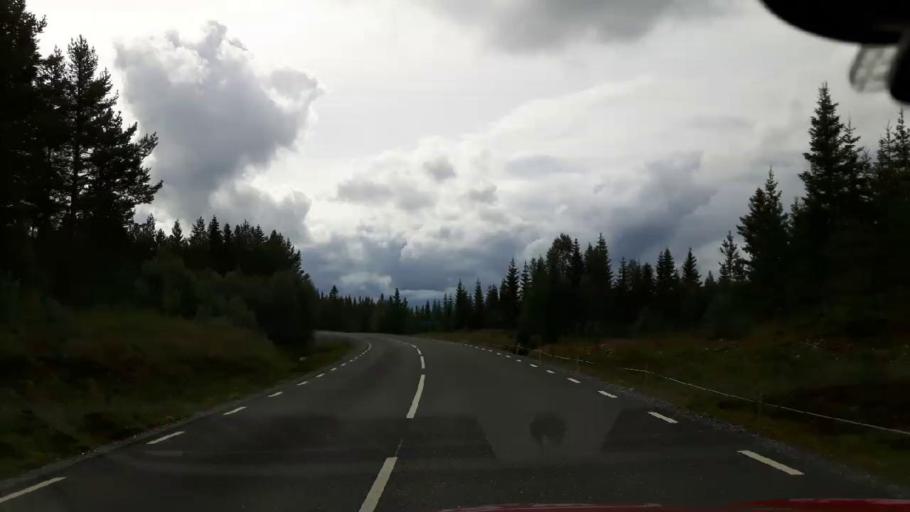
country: NO
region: Nord-Trondelag
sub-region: Lierne
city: Sandvika
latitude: 64.6265
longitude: 14.1232
